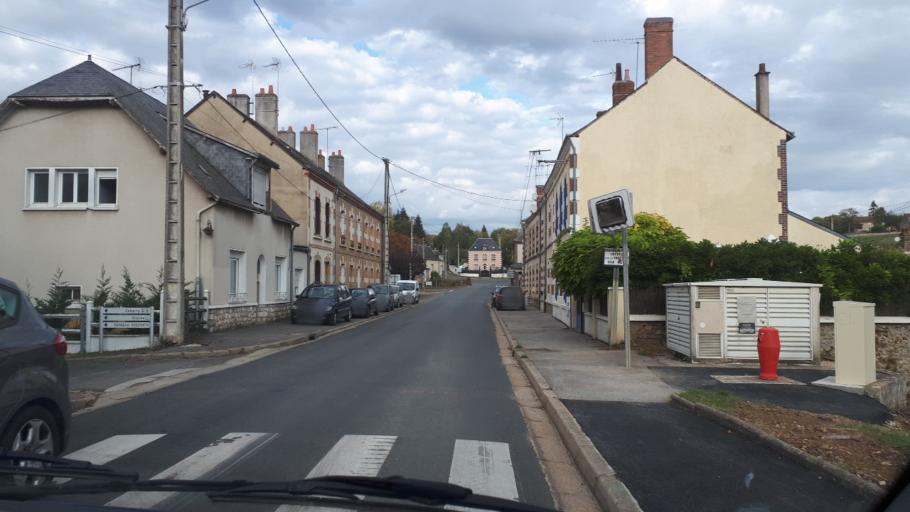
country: FR
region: Centre
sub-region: Departement du Loir-et-Cher
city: Mondoubleau
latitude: 47.9844
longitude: 0.8951
